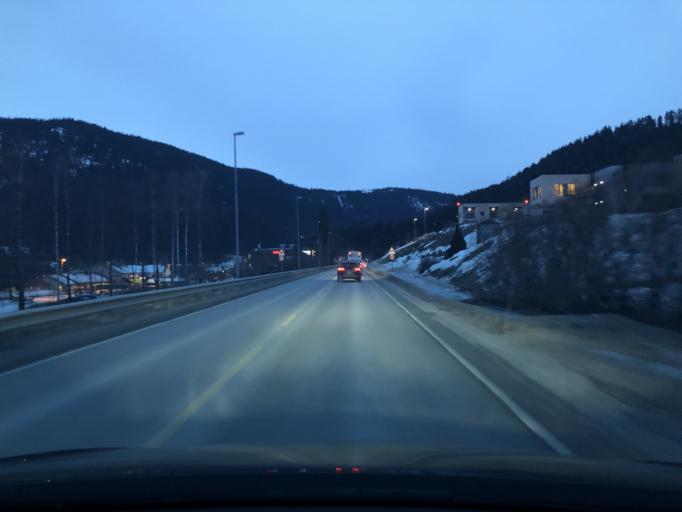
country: NO
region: Oppland
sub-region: Nord-Aurdal
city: Fagernes
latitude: 60.9858
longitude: 9.2426
